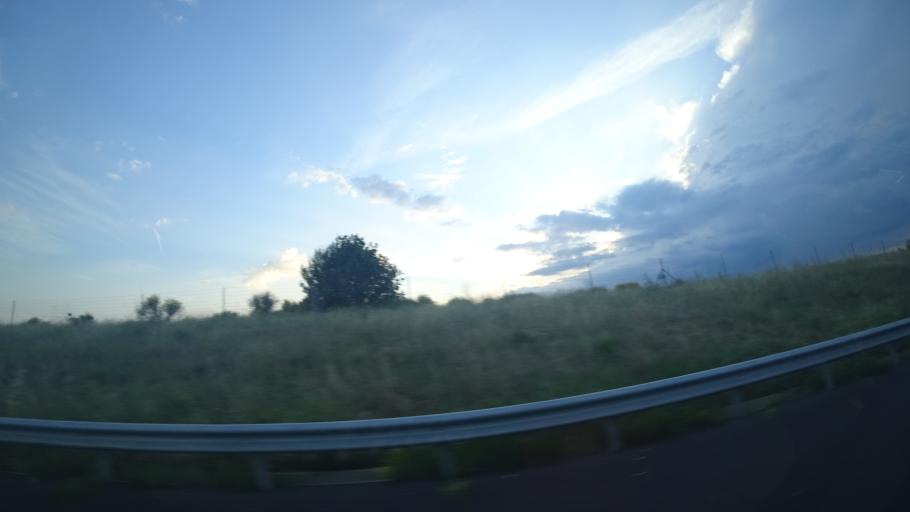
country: FR
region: Languedoc-Roussillon
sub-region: Departement de l'Herault
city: Lezignan-la-Cebe
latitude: 43.5058
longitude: 3.4437
